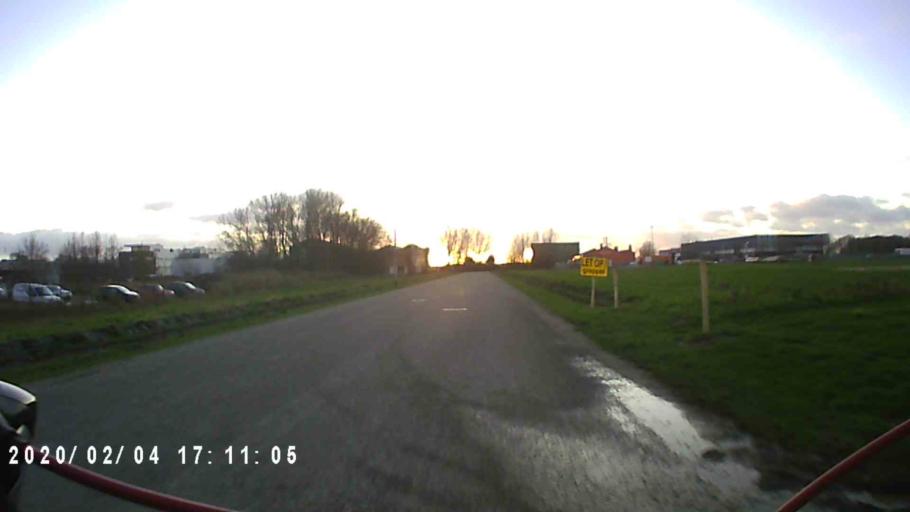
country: NL
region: Groningen
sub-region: Gemeente Groningen
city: Korrewegwijk
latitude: 53.2456
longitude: 6.5324
